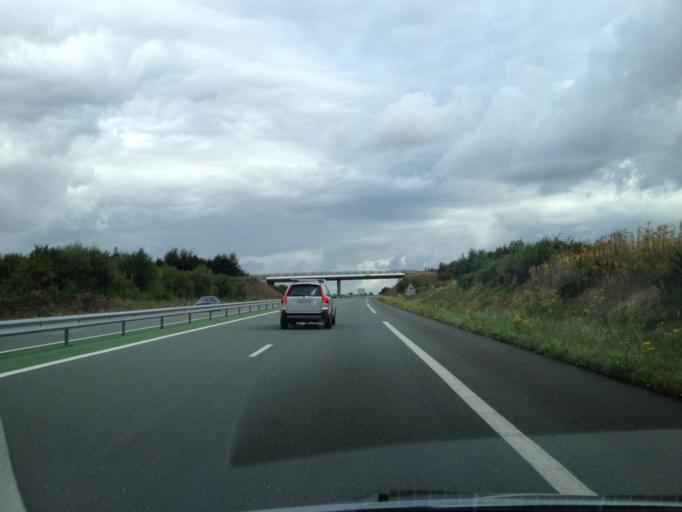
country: FR
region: Pays de la Loire
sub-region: Departement de la Vendee
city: Saint-Fulgent
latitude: 46.8551
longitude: -1.1436
